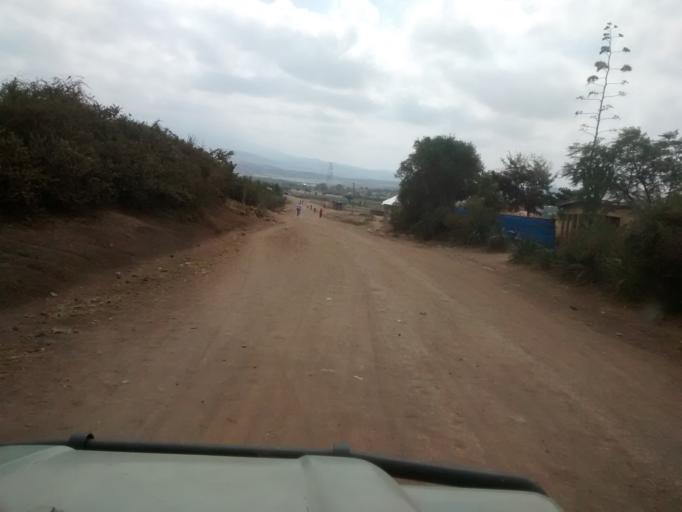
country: TZ
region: Arusha
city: Arusha
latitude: -3.3878
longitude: 36.5907
